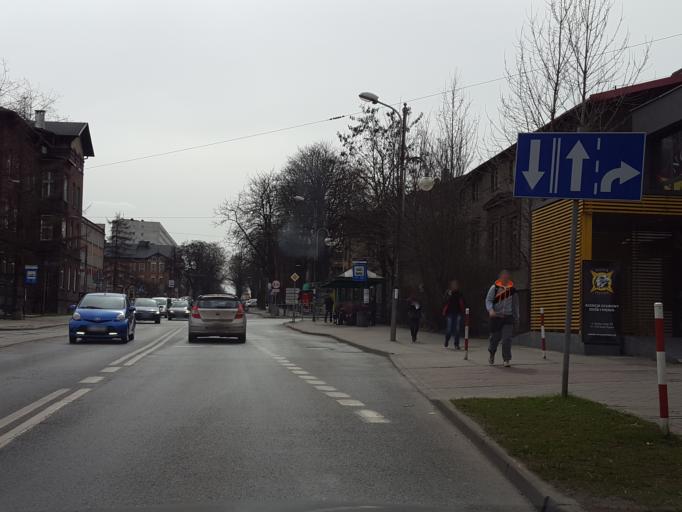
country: PL
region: Silesian Voivodeship
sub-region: Ruda Slaska
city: Ruda Slaska
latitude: 50.2897
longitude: 18.8747
